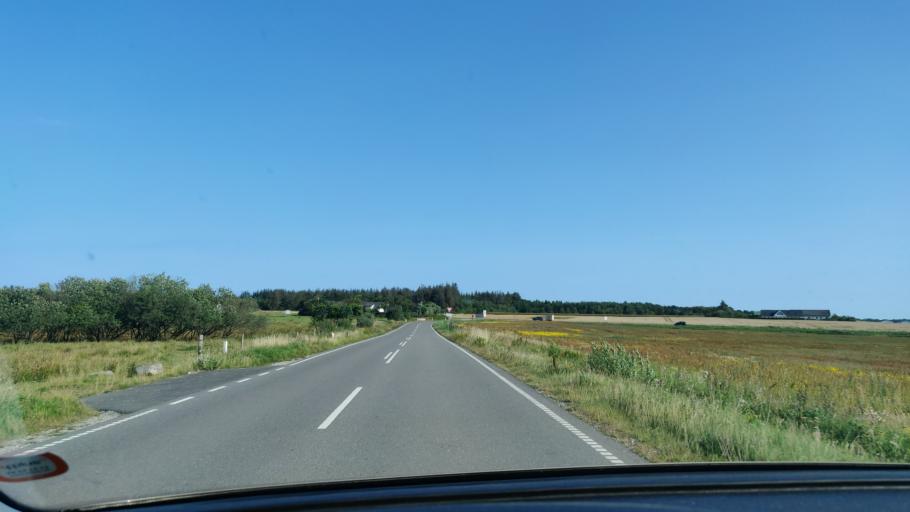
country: DK
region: North Denmark
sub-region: Jammerbugt Kommune
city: Pandrup
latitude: 57.2434
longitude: 9.6472
